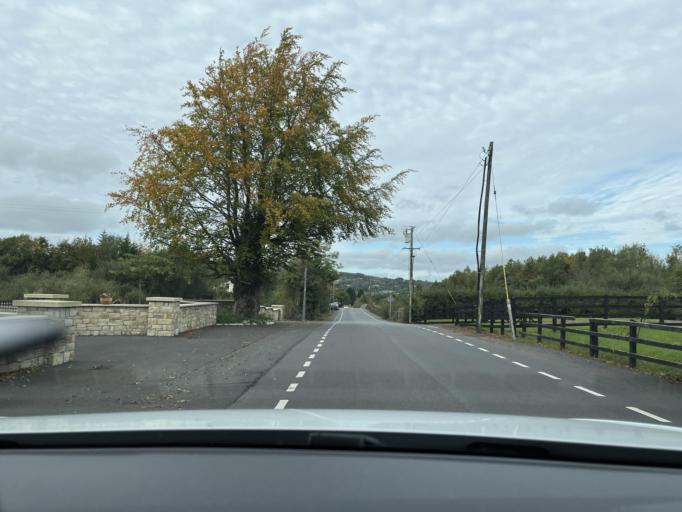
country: IE
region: Connaught
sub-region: Roscommon
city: Boyle
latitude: 53.9777
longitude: -8.2765
